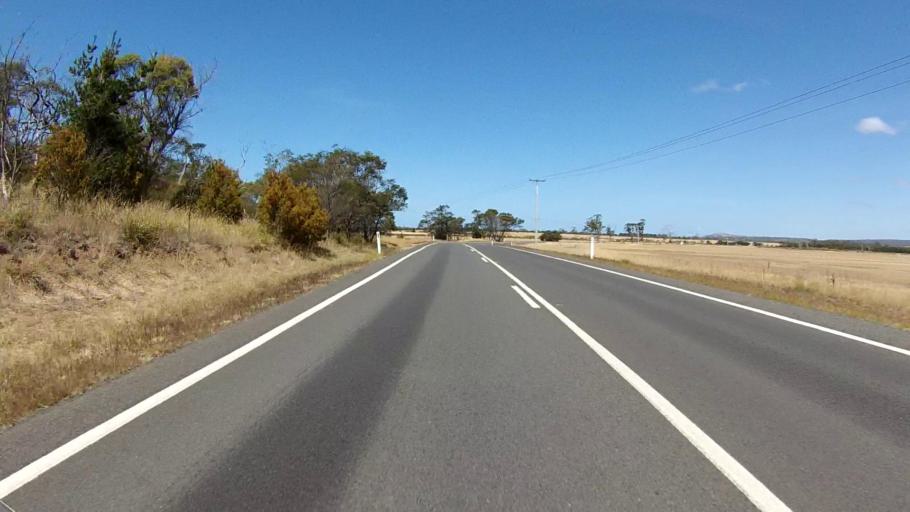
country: AU
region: Tasmania
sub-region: Break O'Day
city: St Helens
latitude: -42.0867
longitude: 148.0666
